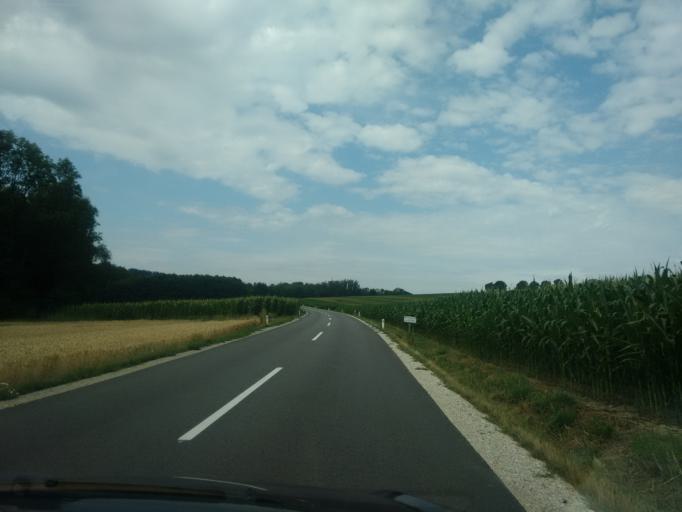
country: AT
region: Upper Austria
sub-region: Politischer Bezirk Grieskirchen
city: Grieskirchen
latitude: 48.2004
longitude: 13.8459
